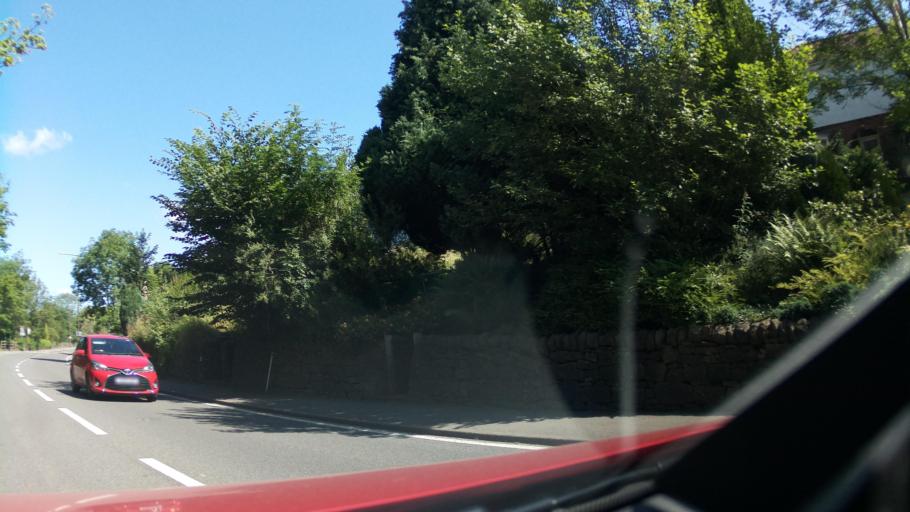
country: GB
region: England
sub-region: Derbyshire
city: Belper
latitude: 53.0137
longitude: -1.4822
